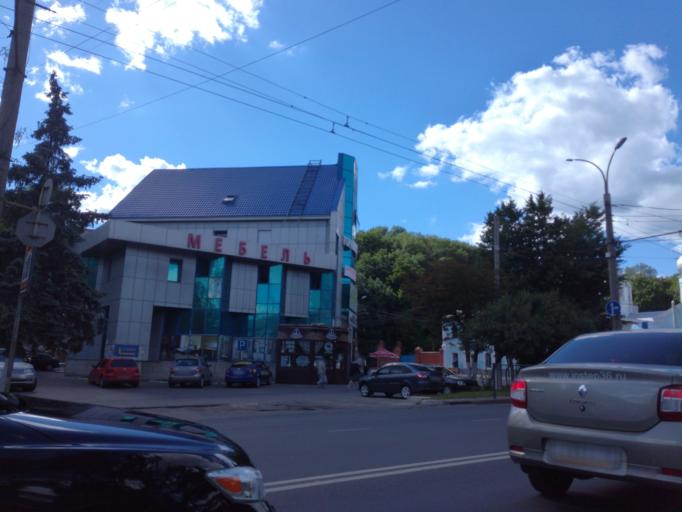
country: RU
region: Kursk
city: Kursk
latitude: 51.7545
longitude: 36.1896
